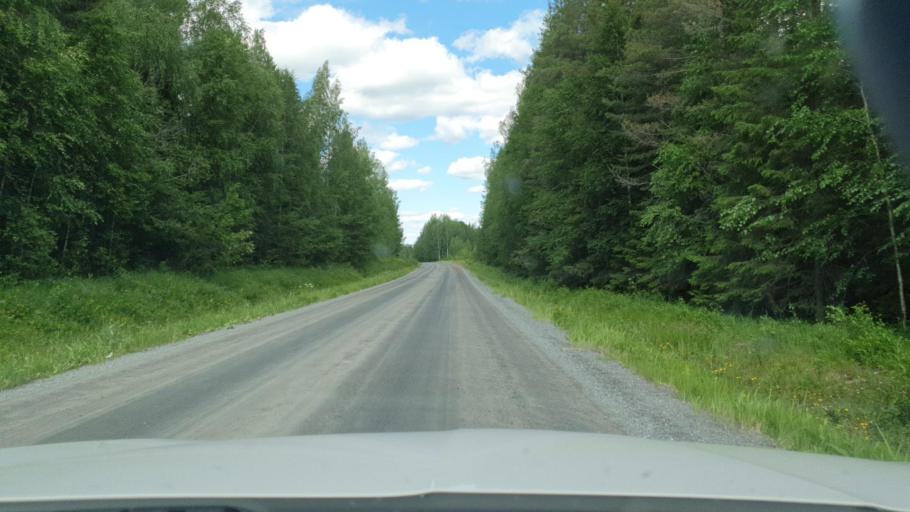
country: SE
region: Vaesterbotten
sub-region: Skelleftea Kommun
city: Forsbacka
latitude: 64.8295
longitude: 20.4998
